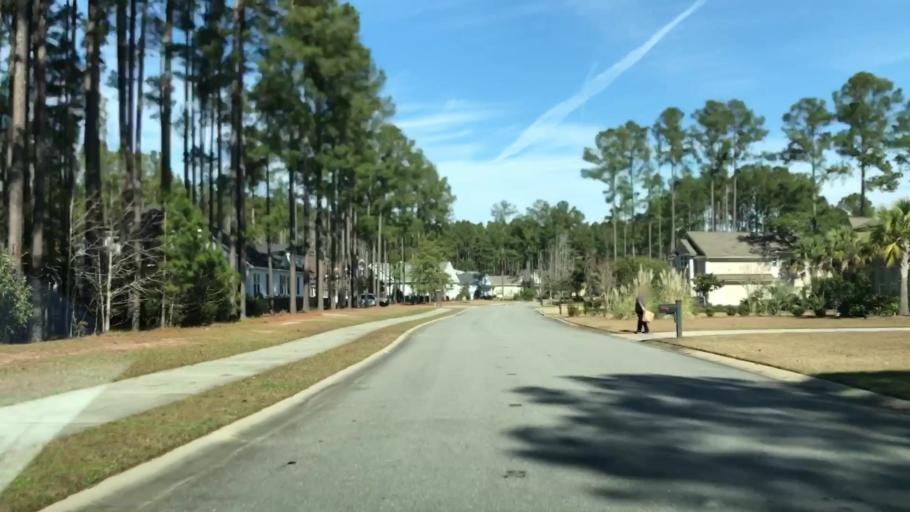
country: US
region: South Carolina
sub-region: Beaufort County
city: Bluffton
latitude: 32.2490
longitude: -80.9309
